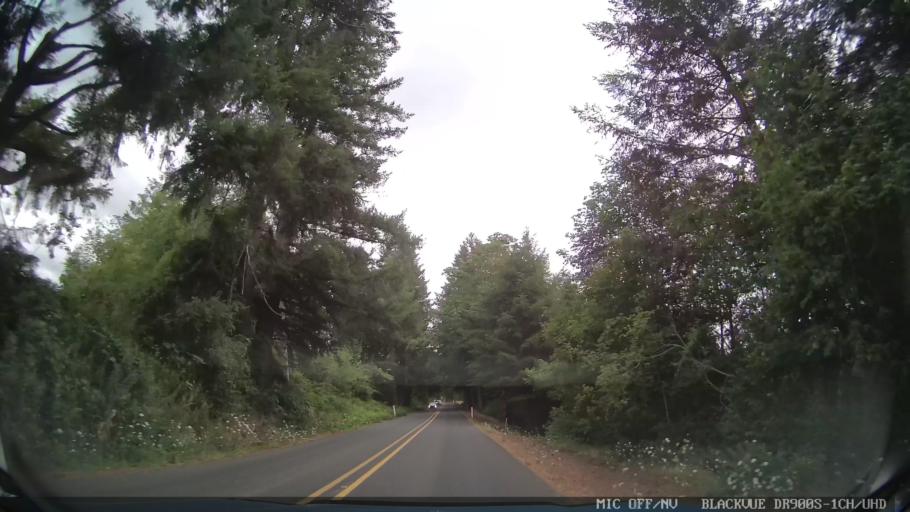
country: US
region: Oregon
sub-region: Linn County
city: Lyons
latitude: 44.8488
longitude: -122.6729
